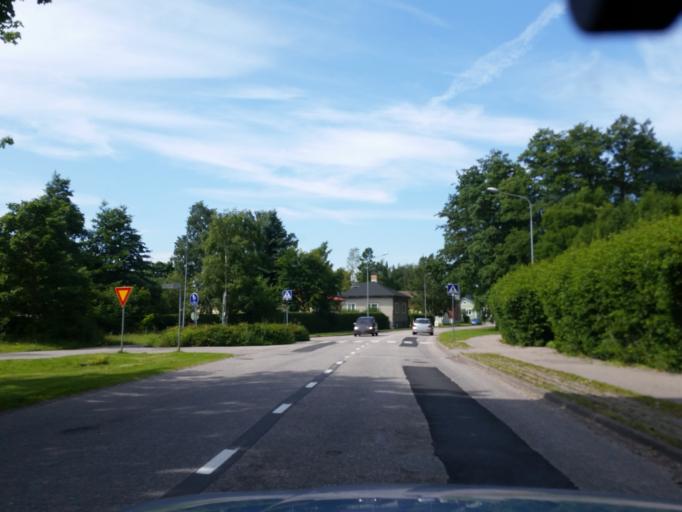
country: FI
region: Uusimaa
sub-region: Raaseporin
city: Hanko
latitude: 59.8337
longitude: 22.9635
